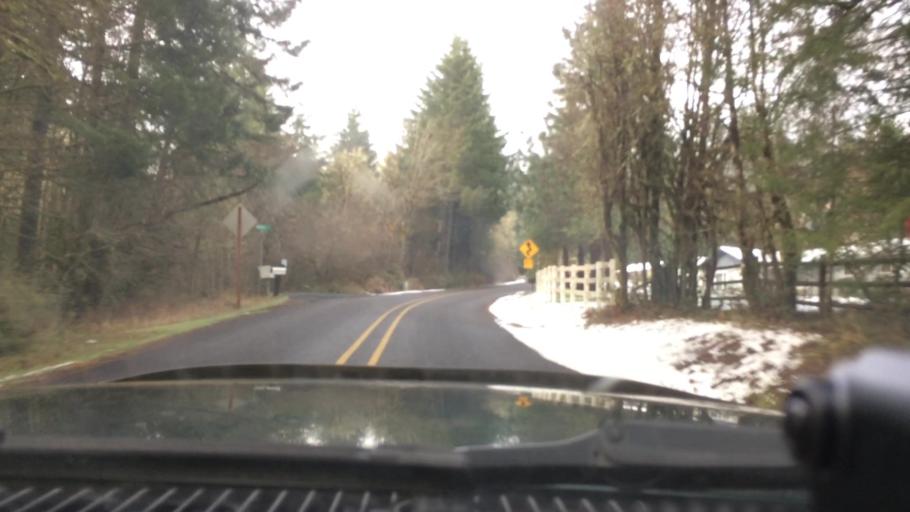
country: US
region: Oregon
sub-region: Lane County
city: Veneta
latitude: 44.1360
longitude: -123.3562
